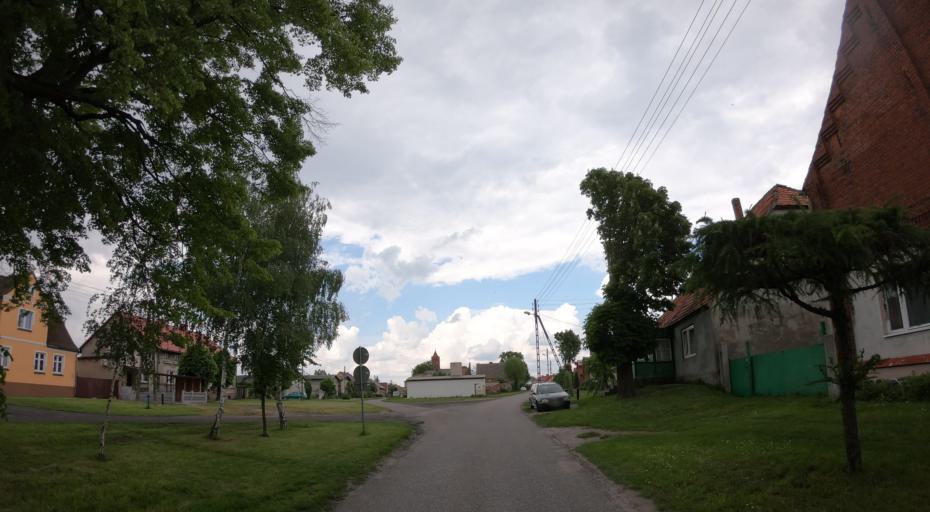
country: PL
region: West Pomeranian Voivodeship
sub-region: Powiat pyrzycki
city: Bielice
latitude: 53.2274
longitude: 14.7666
